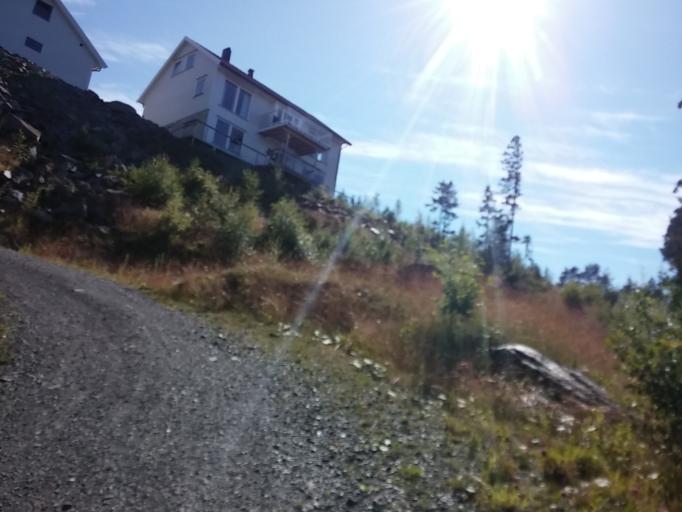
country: NO
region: Sor-Trondelag
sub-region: Malvik
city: Hommelvik
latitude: 63.4296
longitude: 10.7525
